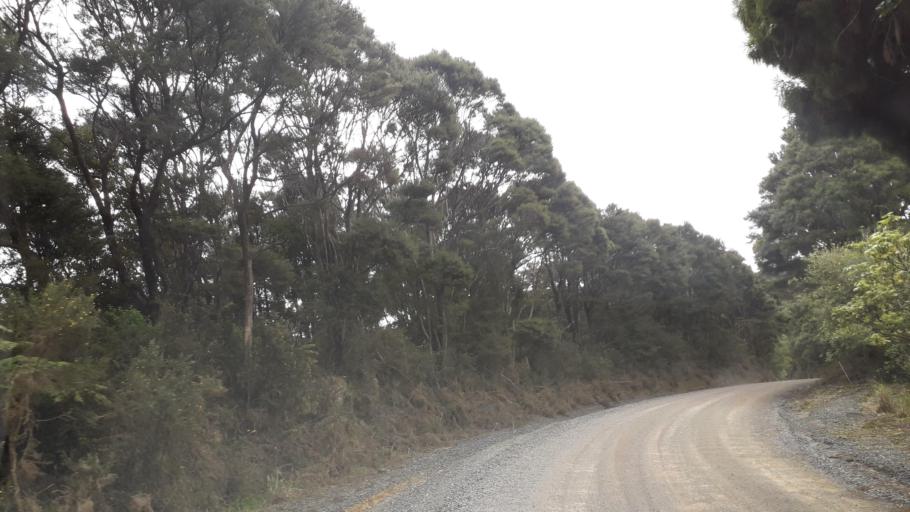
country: NZ
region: Northland
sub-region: Far North District
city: Paihia
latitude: -35.3169
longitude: 174.2264
